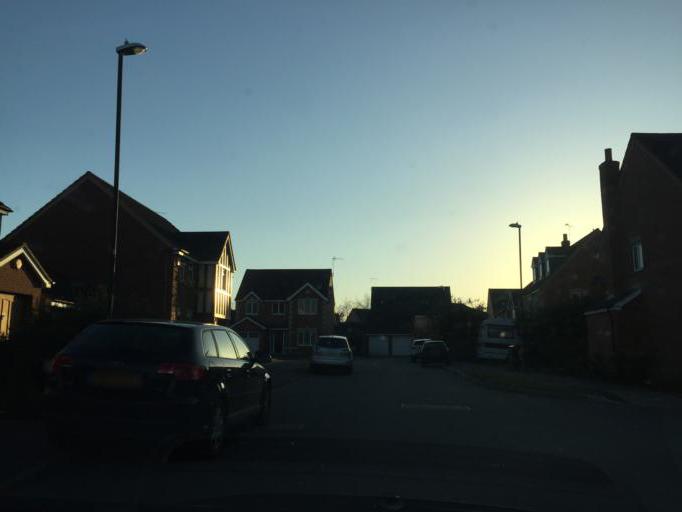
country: GB
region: England
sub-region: Warwickshire
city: Ryton on Dunsmore
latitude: 52.3993
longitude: -1.4341
